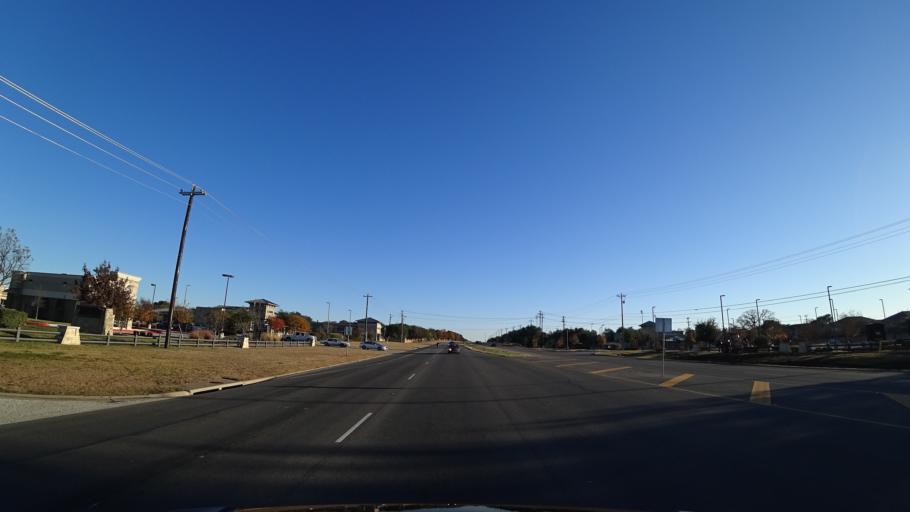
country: US
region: Texas
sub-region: Williamson County
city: Brushy Creek
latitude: 30.4975
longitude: -97.7753
